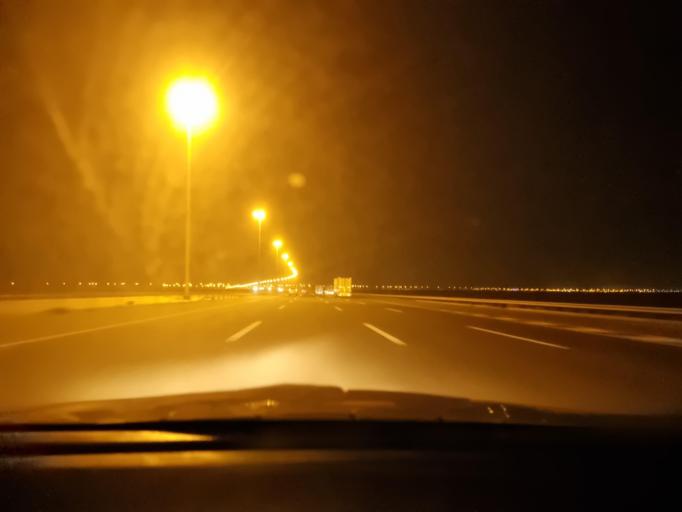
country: AE
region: Dubai
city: Dubai
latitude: 24.7041
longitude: 54.8432
